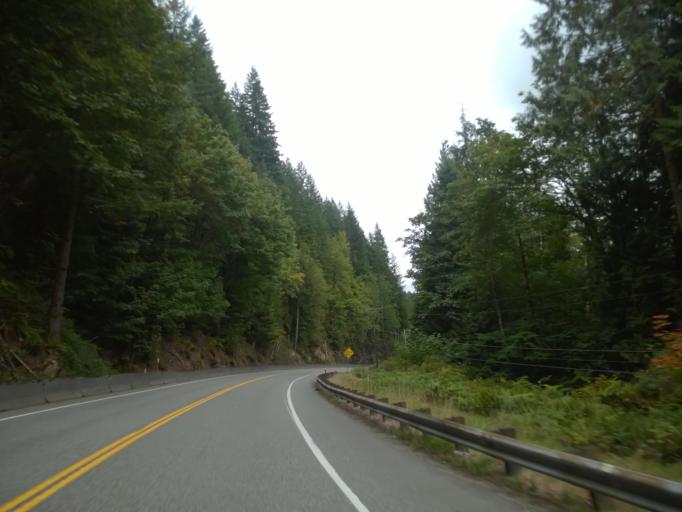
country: US
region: Washington
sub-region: Snohomish County
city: Gold Bar
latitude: 47.8035
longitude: -121.5166
